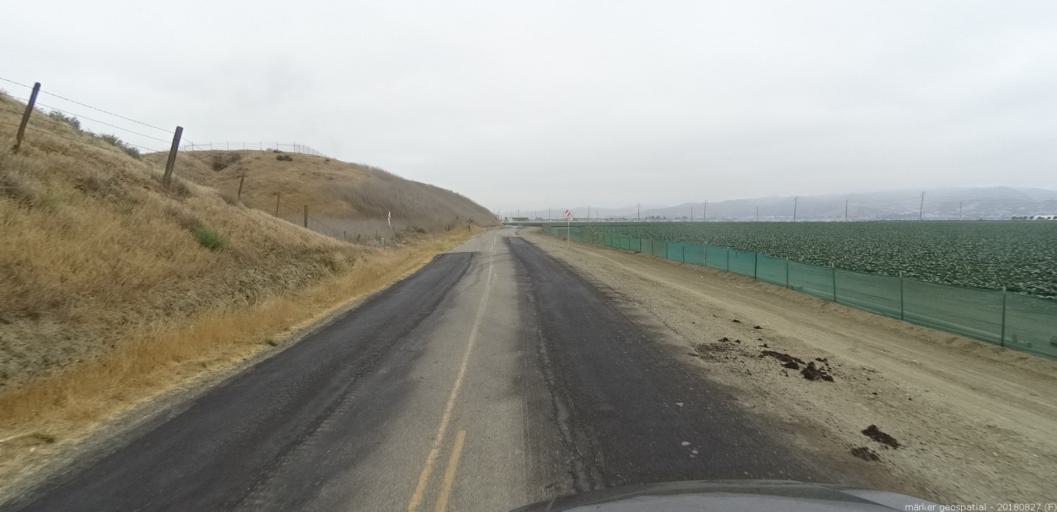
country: US
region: California
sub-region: Monterey County
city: King City
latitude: 36.2349
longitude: -121.1284
